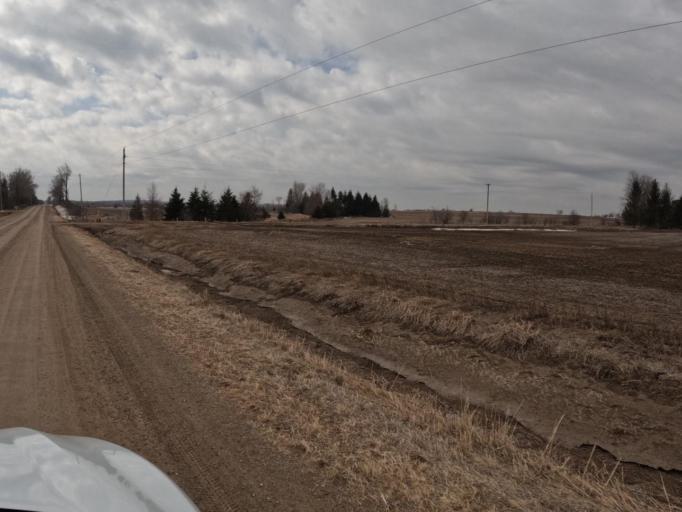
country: CA
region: Ontario
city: Orangeville
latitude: 43.9228
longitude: -80.1861
